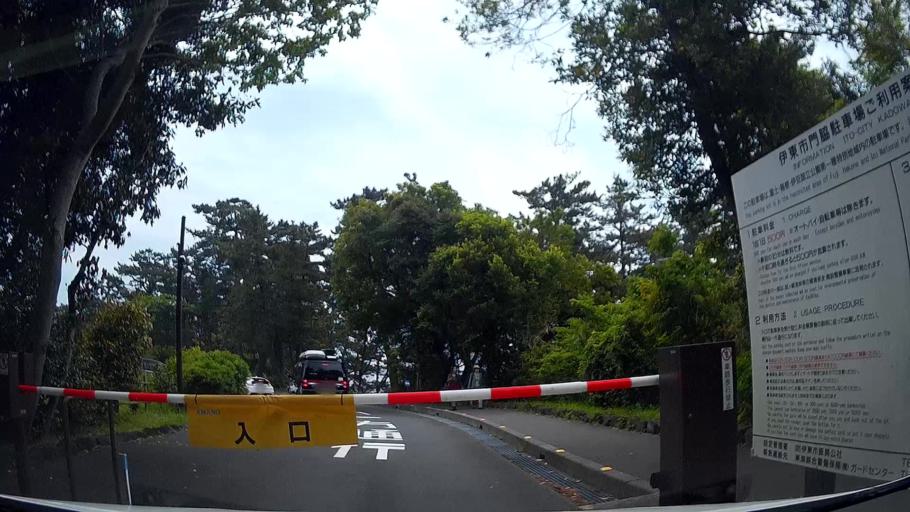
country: JP
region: Shizuoka
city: Ito
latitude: 34.8909
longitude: 139.1366
